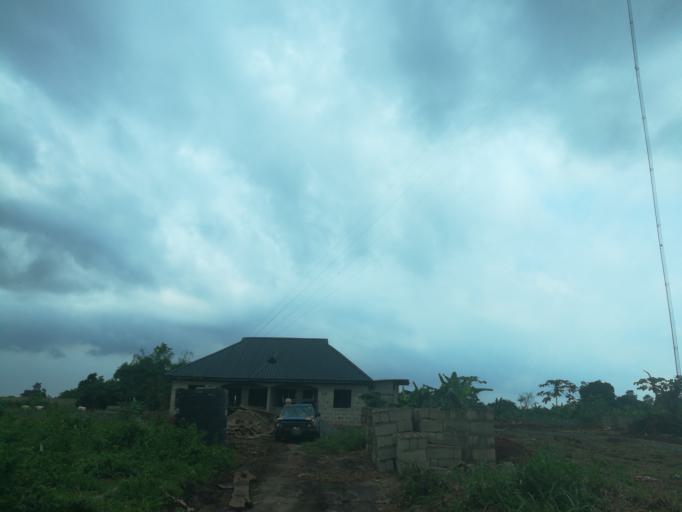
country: NG
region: Lagos
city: Ikorodu
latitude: 6.6640
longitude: 3.6164
